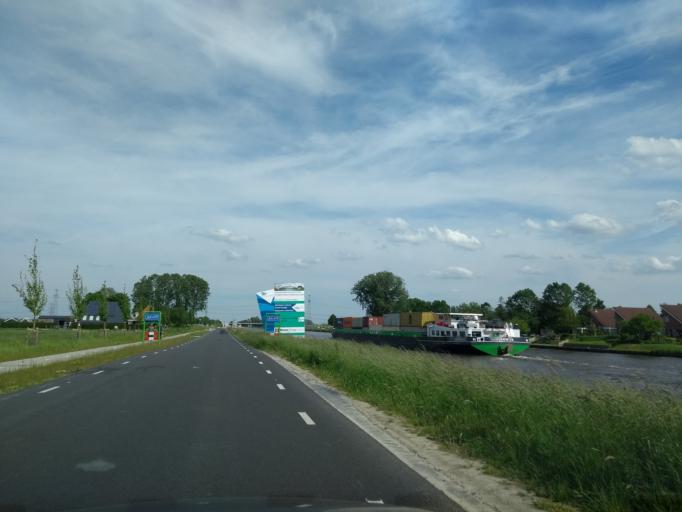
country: NL
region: Groningen
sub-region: Gemeente Zuidhorn
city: Aduard
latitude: 53.2612
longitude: 6.4596
